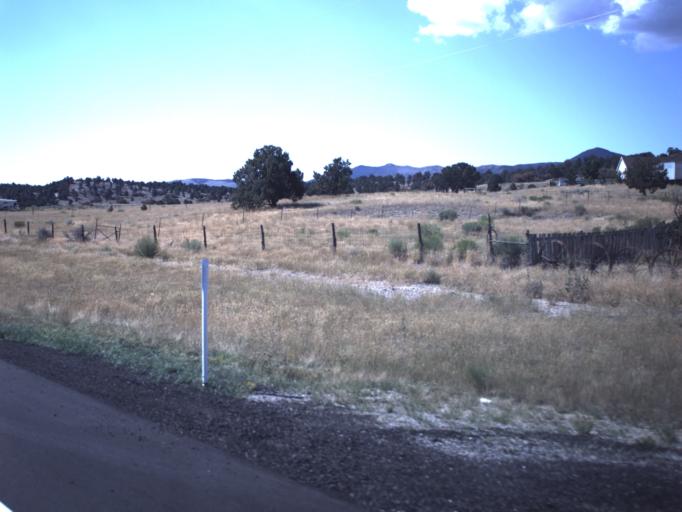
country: US
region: Utah
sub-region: Utah County
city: Eagle Mountain
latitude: 40.0258
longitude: -112.2820
